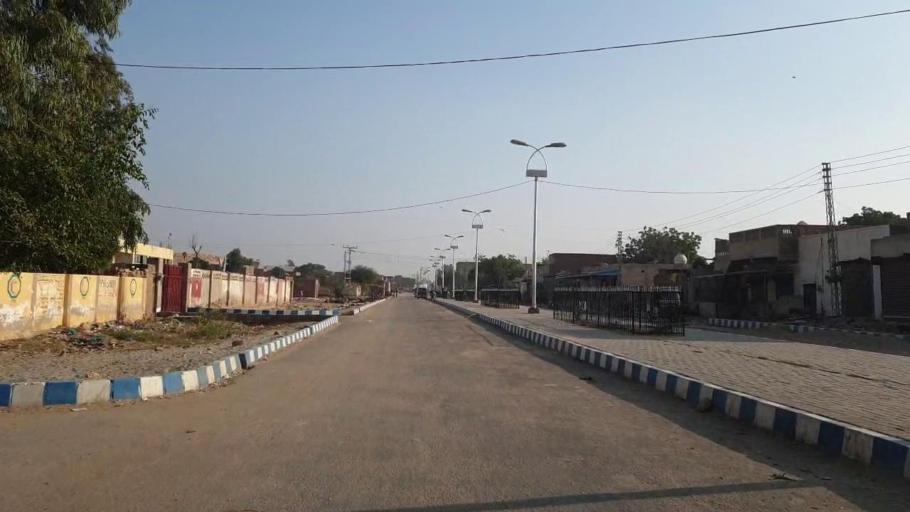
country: PK
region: Sindh
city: Kotri
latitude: 25.3618
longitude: 68.2600
